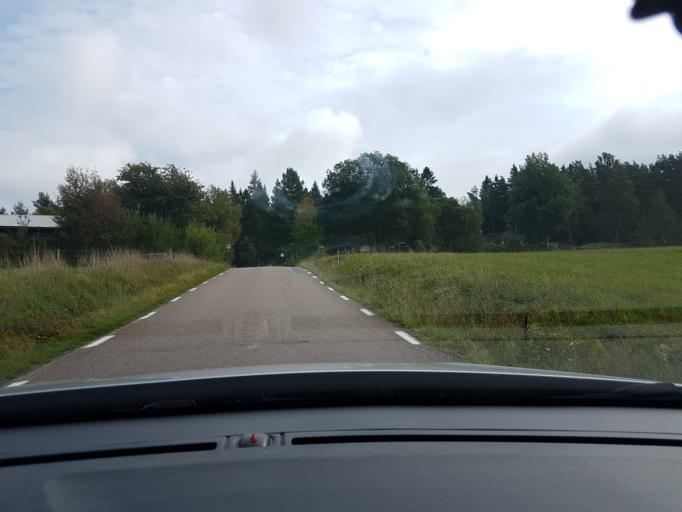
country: SE
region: Vaestra Goetaland
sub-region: Ale Kommun
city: Alvangen
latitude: 57.9080
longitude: 12.1635
